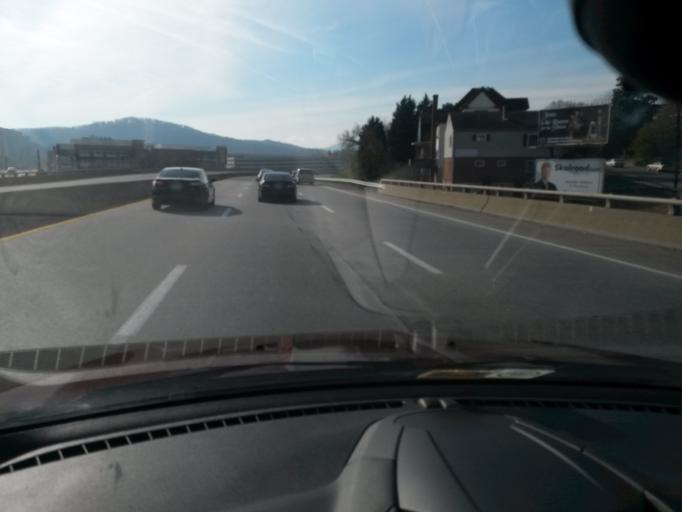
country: US
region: Virginia
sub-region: City of Roanoke
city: Cedar Bluff
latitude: 37.2607
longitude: -79.9415
